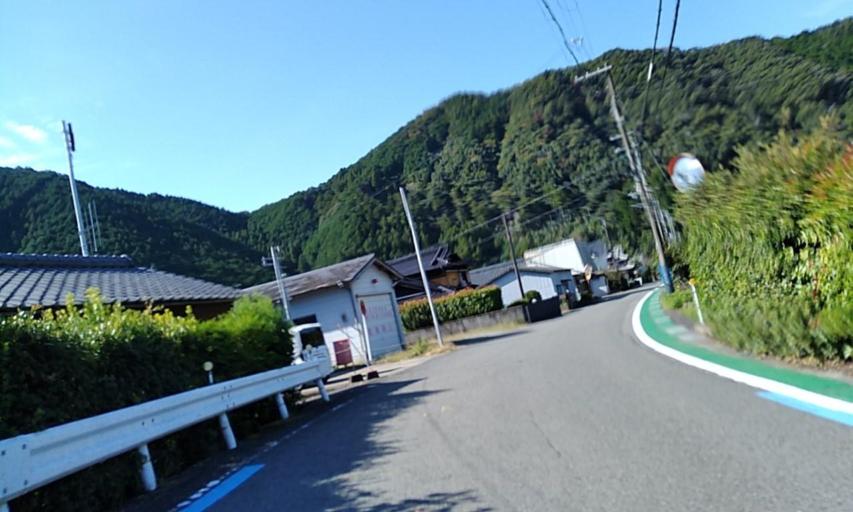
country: JP
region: Wakayama
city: Kainan
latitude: 34.0479
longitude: 135.3144
